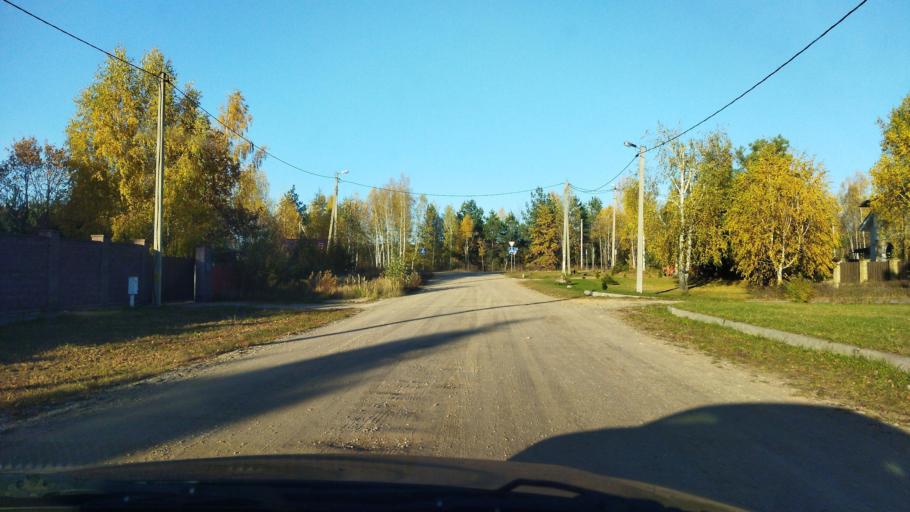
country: BY
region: Minsk
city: Kalodzishchy
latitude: 53.9138
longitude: 27.7719
